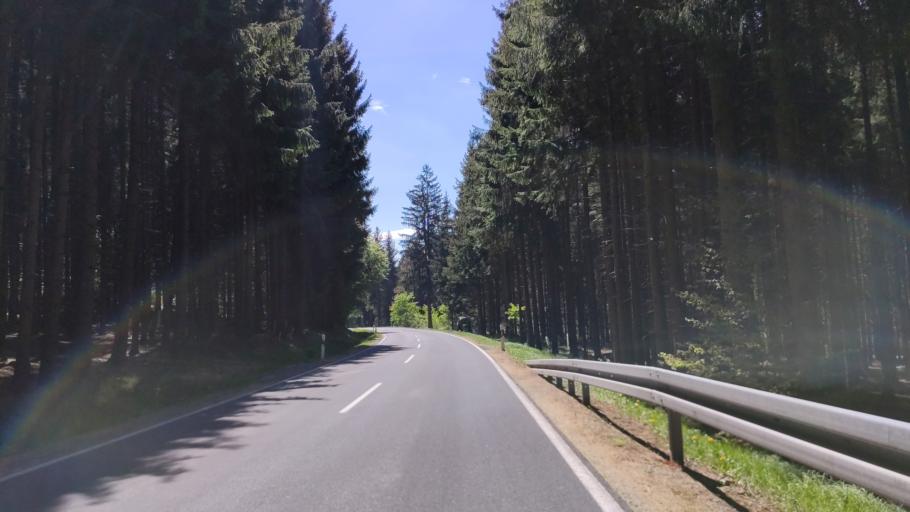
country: DE
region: Bavaria
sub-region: Upper Franconia
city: Reichenbach
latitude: 50.4425
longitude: 11.4144
